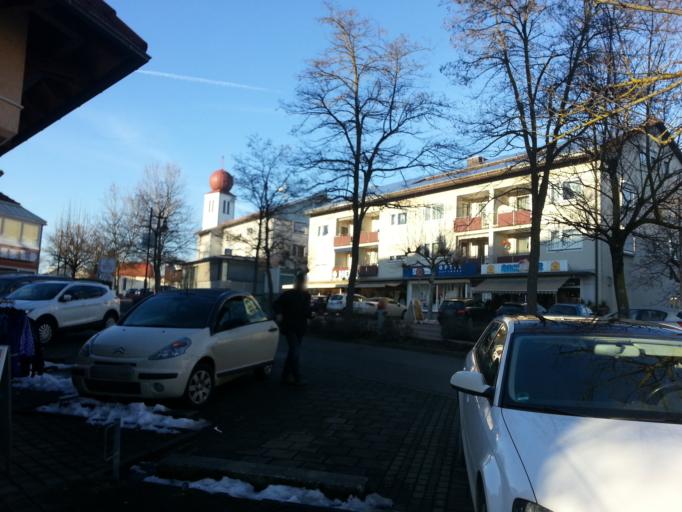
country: DE
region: Baden-Wuerttemberg
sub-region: Tuebingen Region
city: Kressbronn am Bodensee
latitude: 47.5954
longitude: 9.5997
